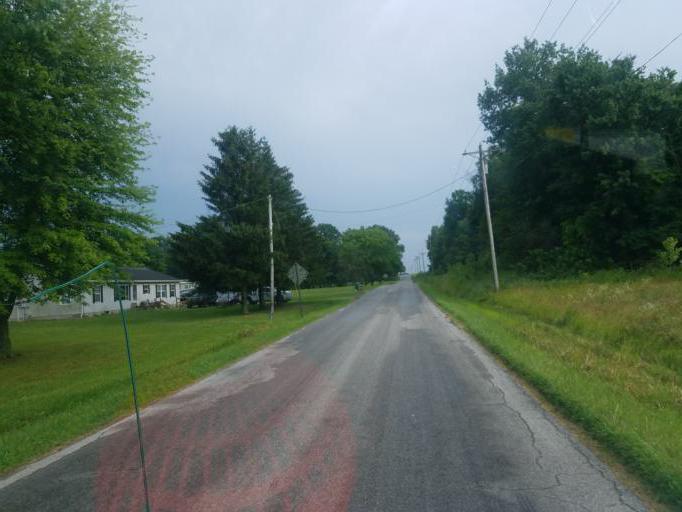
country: US
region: Ohio
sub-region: Wayne County
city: West Salem
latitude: 40.9217
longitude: -82.0812
